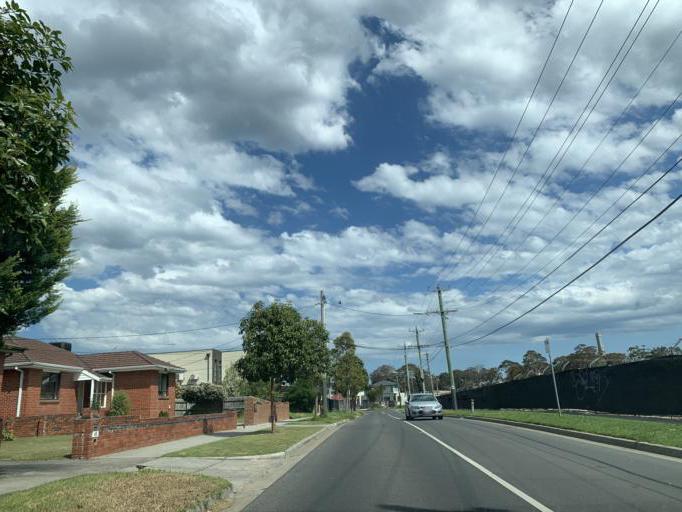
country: AU
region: Victoria
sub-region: Bayside
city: Highett
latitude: -37.9506
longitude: 145.0416
